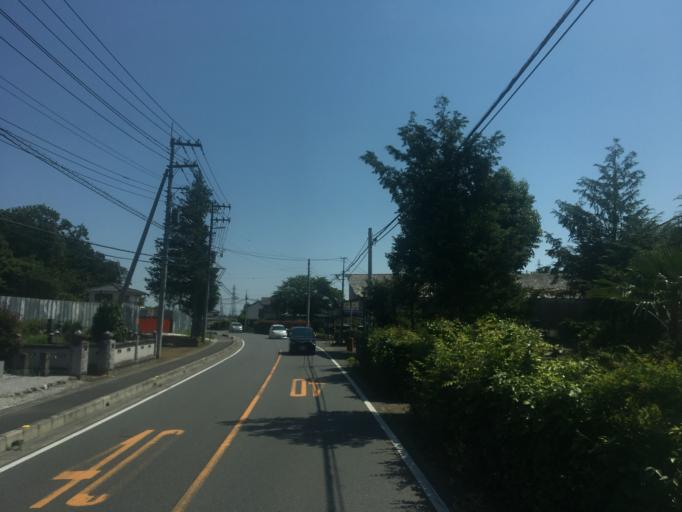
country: JP
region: Saitama
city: Ogawa
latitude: 36.0208
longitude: 139.3193
